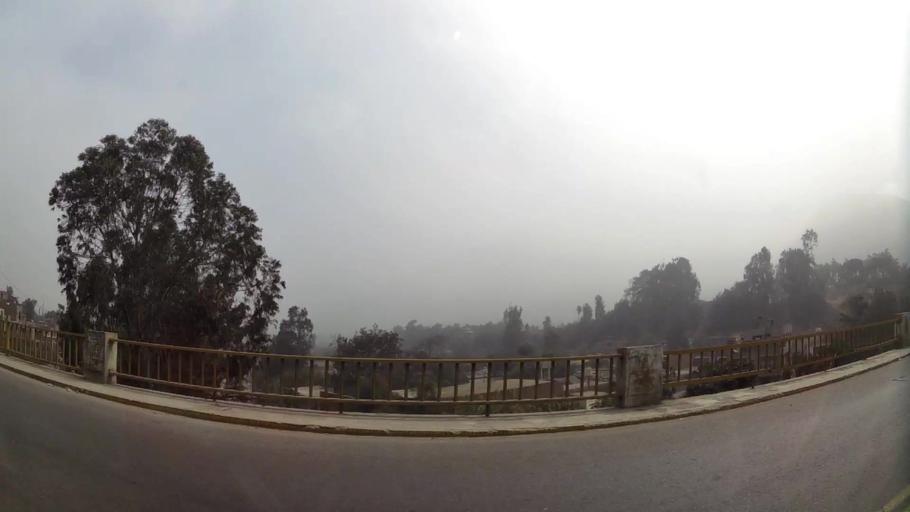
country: PE
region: Lima
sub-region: Lima
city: Chaclacayo
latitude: -11.9677
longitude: -76.7455
